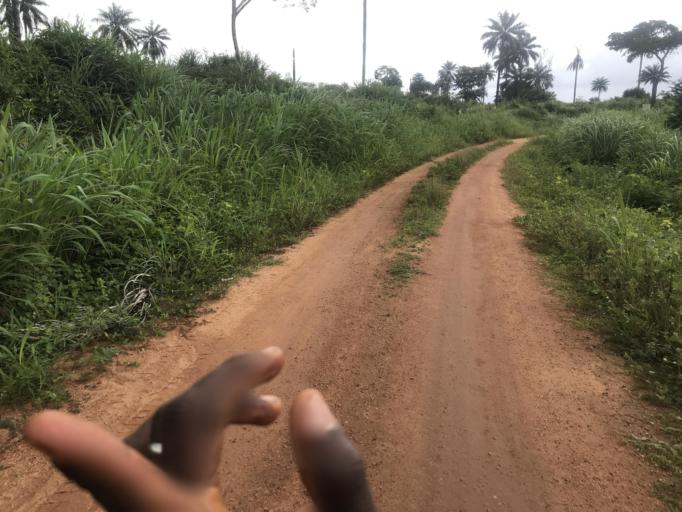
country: GN
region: Nzerekore
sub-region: Prefecture de Guekedou
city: Gueckedou
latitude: 8.4779
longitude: -10.2964
